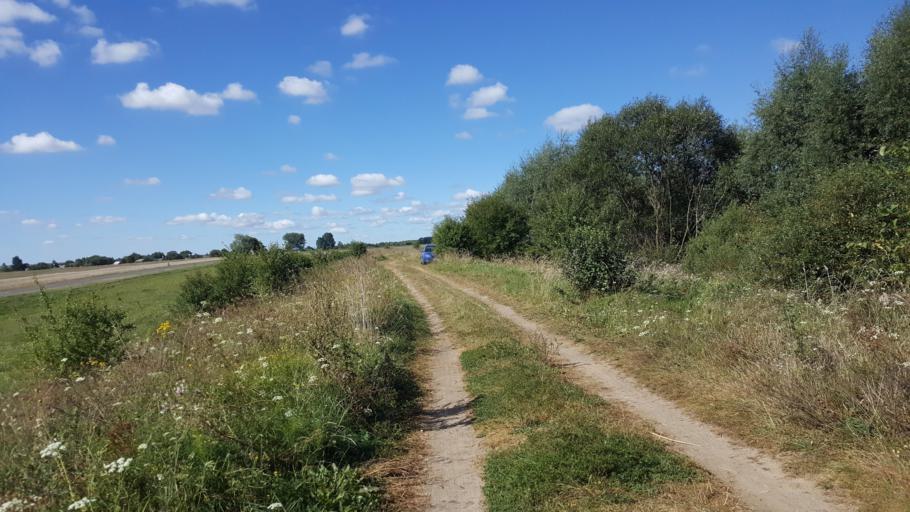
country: BY
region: Brest
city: Vysokaye
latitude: 52.3675
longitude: 23.5317
